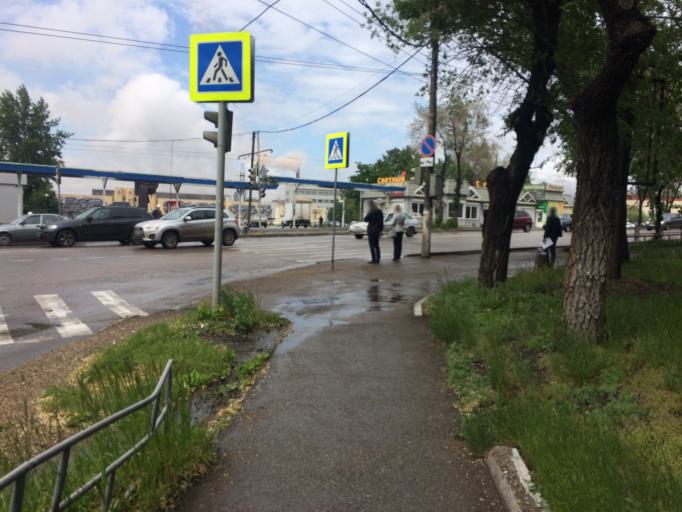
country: RU
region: Chelyabinsk
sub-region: Gorod Magnitogorsk
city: Magnitogorsk
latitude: 53.4138
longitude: 59.0559
